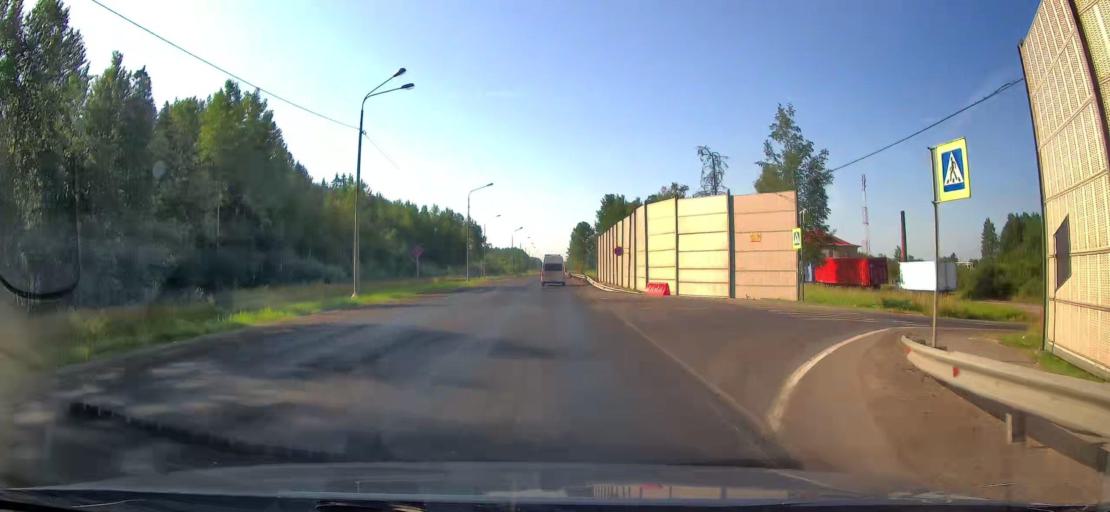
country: RU
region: Leningrad
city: Khvalovo
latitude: 59.9554
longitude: 32.7426
